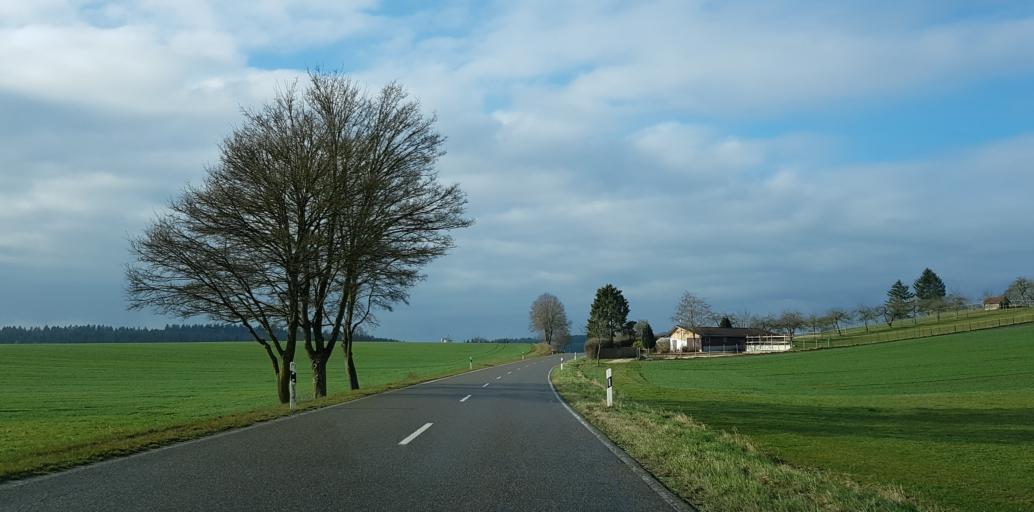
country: DE
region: Baden-Wuerttemberg
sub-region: Tuebingen Region
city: Altheim
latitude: 48.3397
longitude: 9.8100
